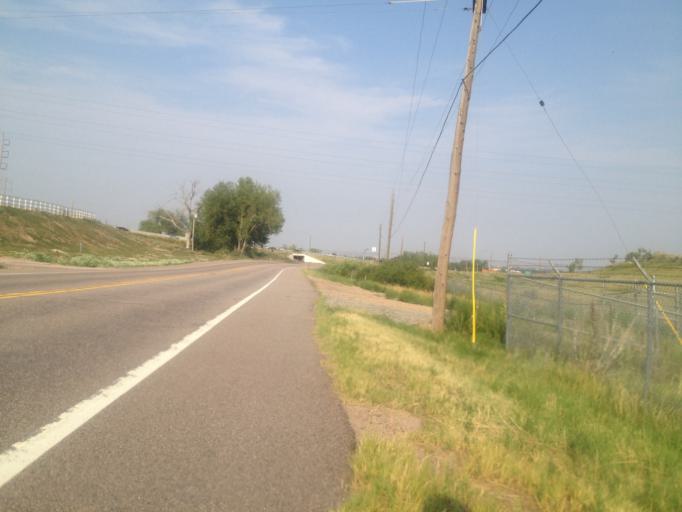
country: US
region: Colorado
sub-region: Boulder County
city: Superior
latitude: 39.9634
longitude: -105.1849
